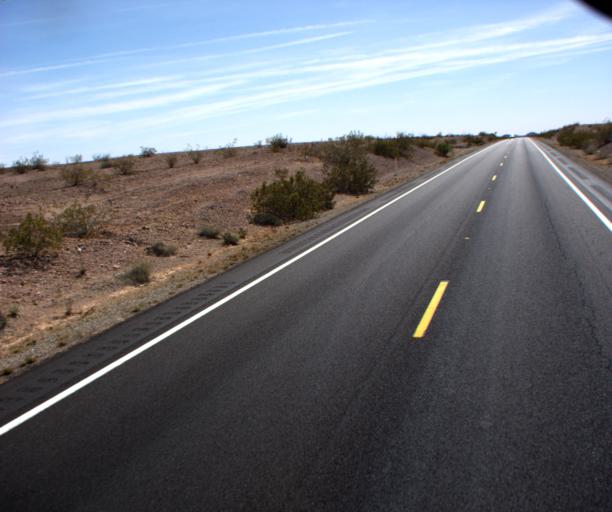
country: US
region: Arizona
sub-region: Yuma County
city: Wellton
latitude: 33.1077
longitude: -114.2962
